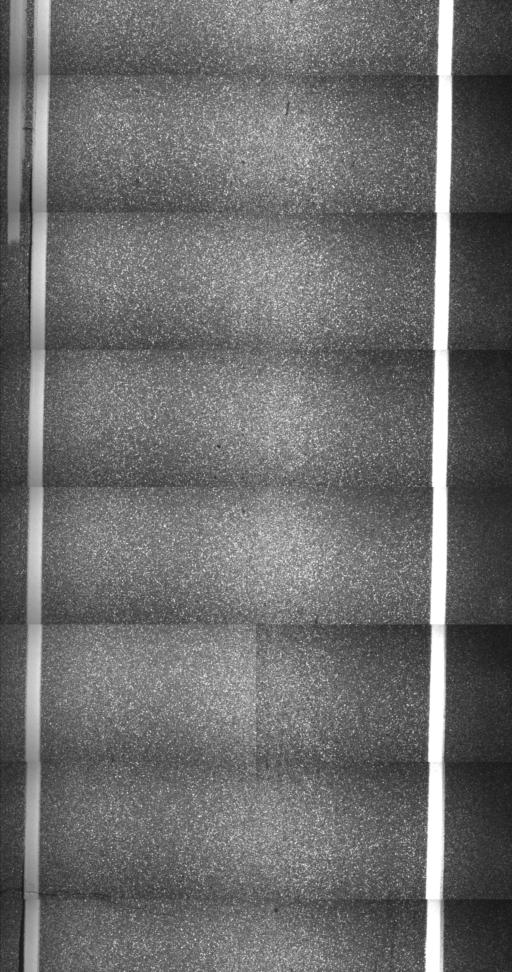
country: US
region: New Hampshire
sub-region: Grafton County
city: Haverhill
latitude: 44.0514
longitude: -72.2176
